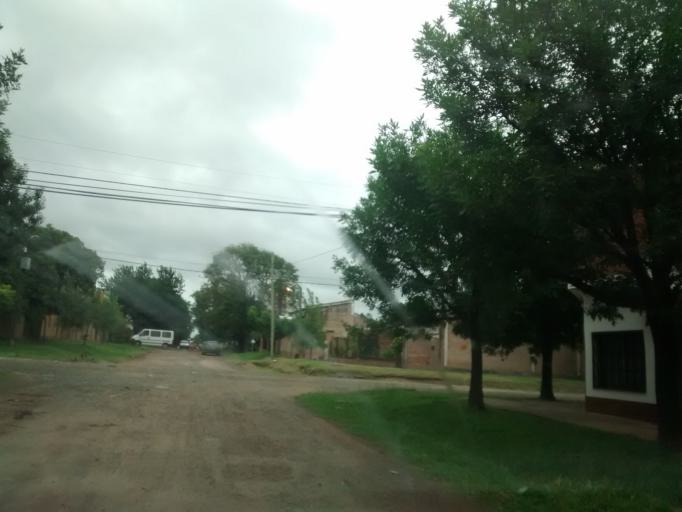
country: AR
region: Chaco
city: Fontana
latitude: -27.4374
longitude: -59.0055
